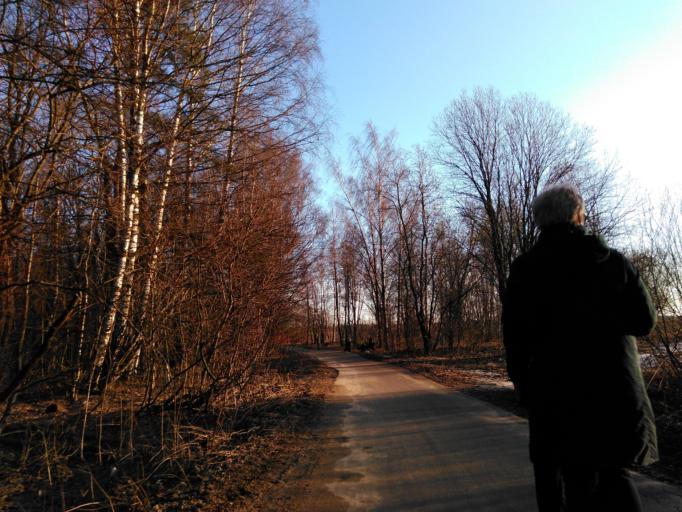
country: RU
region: Moscow
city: Zyuzino
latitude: 55.6356
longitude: 37.5621
